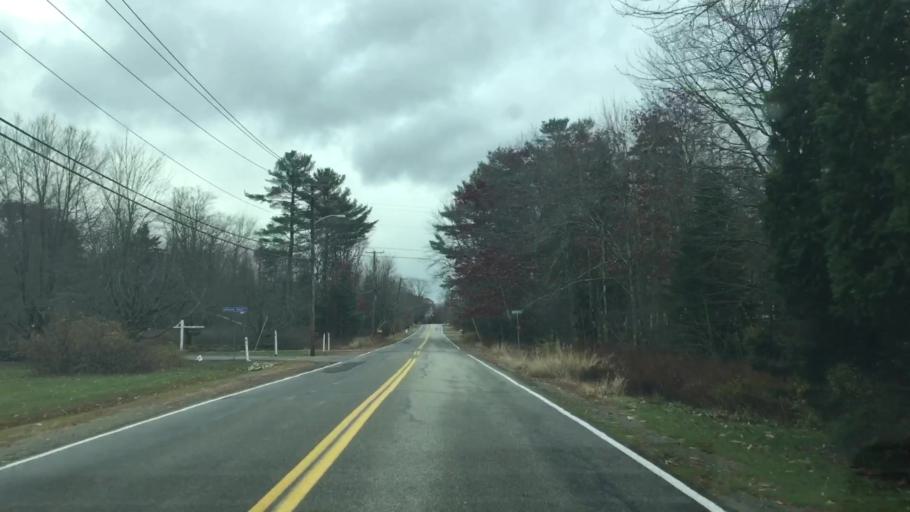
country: US
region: Maine
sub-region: York County
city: Kennebunkport
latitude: 43.3558
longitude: -70.5001
